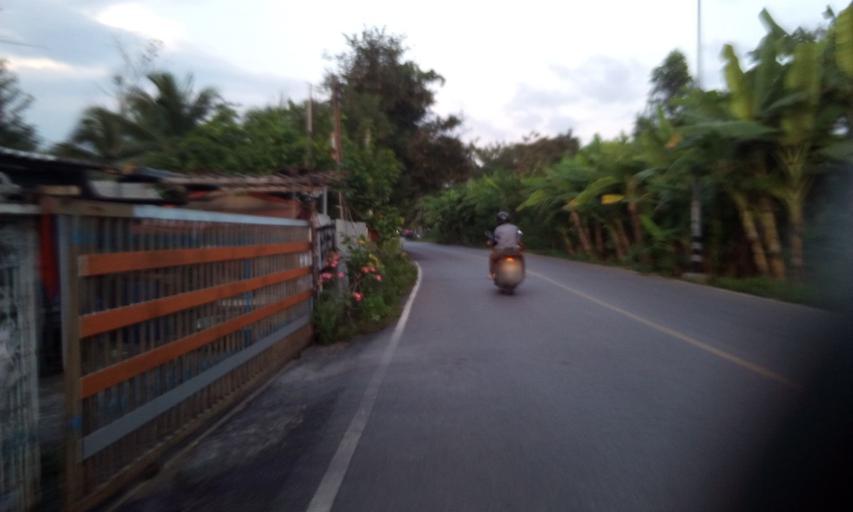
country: TH
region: Pathum Thani
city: Ban Rangsit
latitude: 14.0494
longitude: 100.8171
